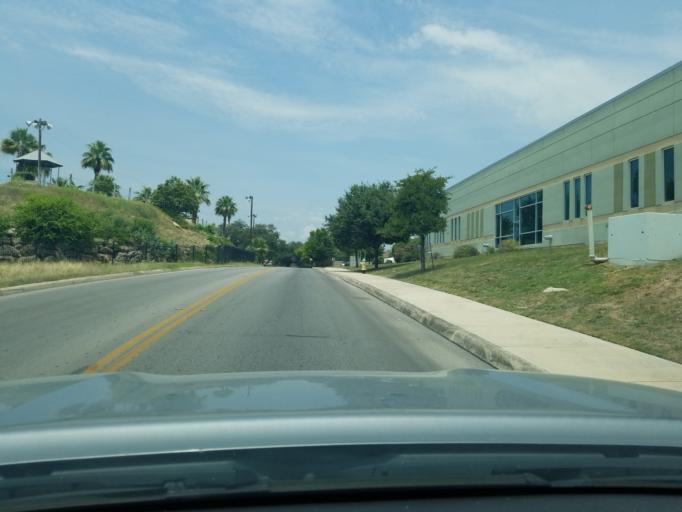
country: US
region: Texas
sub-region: Bexar County
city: Hollywood Park
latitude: 29.5622
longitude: -98.4860
